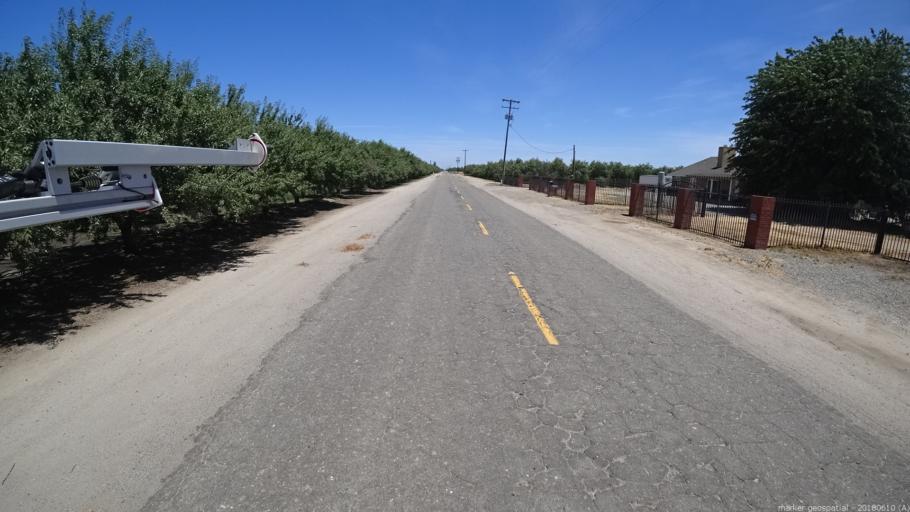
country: US
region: California
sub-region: Madera County
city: Chowchilla
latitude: 37.0617
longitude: -120.2995
